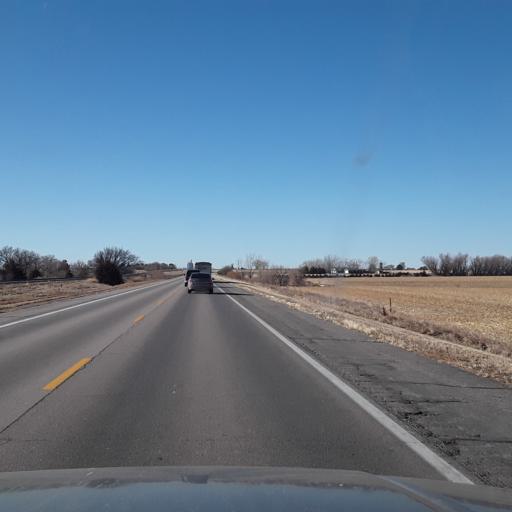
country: US
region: Nebraska
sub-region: Kearney County
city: Minden
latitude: 40.4998
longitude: -98.9719
